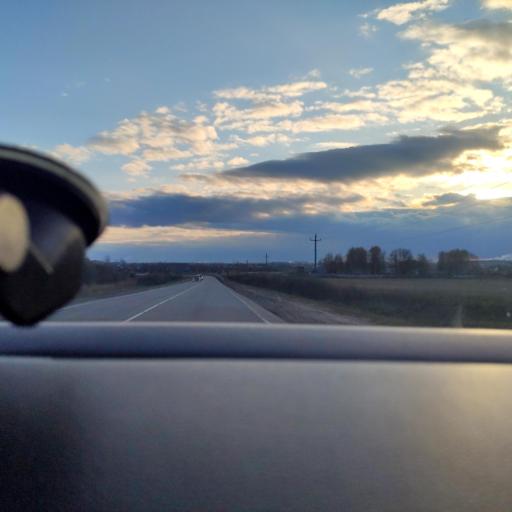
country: RU
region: Moskovskaya
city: Yegor'yevsk
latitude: 55.3923
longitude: 39.0941
